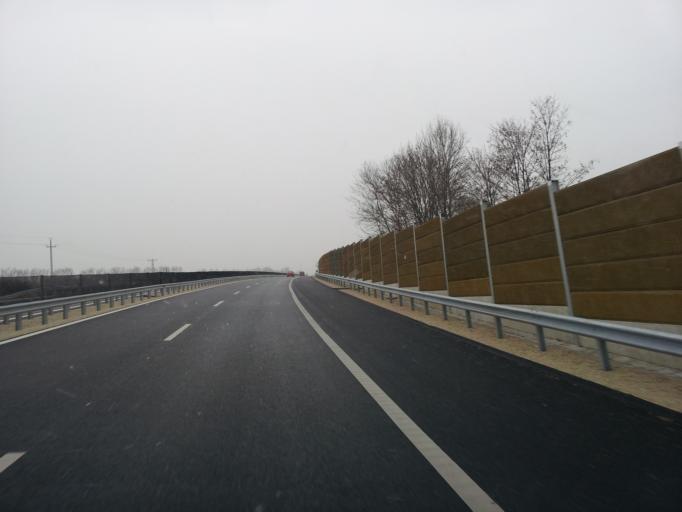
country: HU
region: Veszprem
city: Herend
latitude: 47.1323
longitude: 17.7397
